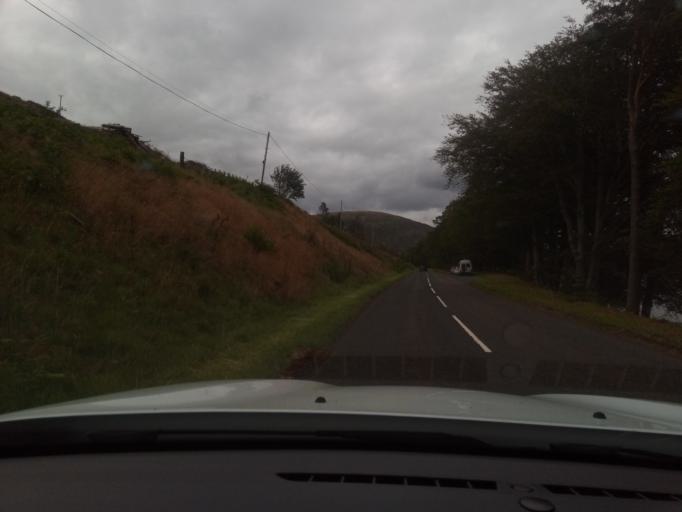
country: GB
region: Scotland
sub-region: The Scottish Borders
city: Peebles
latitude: 55.4797
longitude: -3.2087
